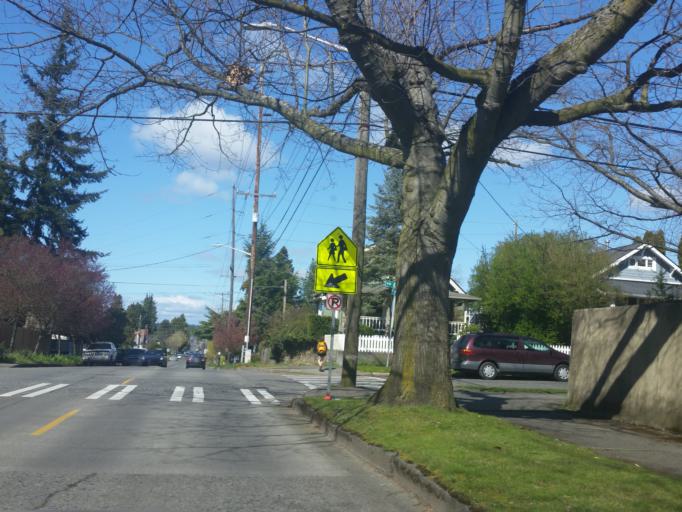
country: US
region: Washington
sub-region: King County
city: Shoreline
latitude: 47.6875
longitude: -122.3606
